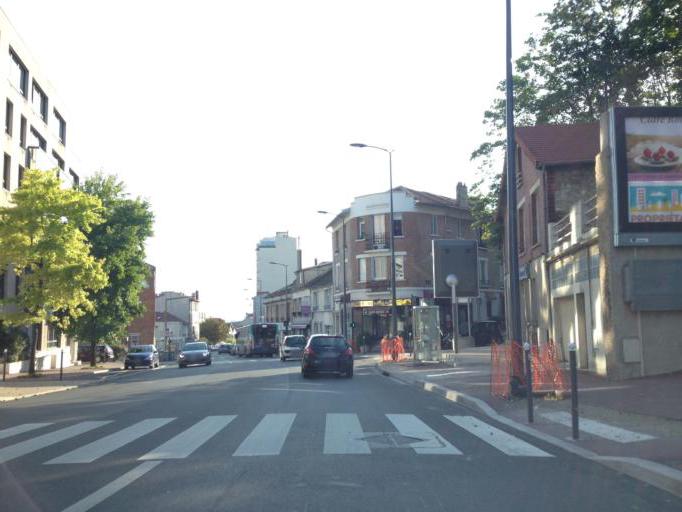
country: FR
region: Ile-de-France
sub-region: Departement des Hauts-de-Seine
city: Boulogne-Billancourt
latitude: 48.8191
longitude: 2.2590
